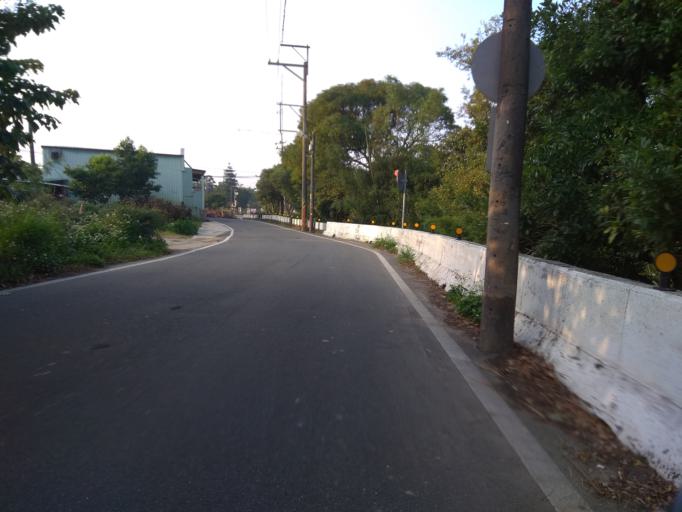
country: TW
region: Taiwan
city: Daxi
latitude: 24.9355
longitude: 121.2103
